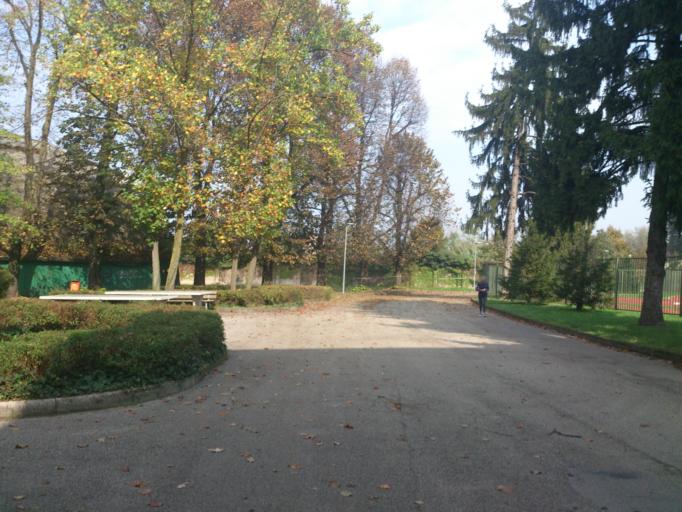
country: IT
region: Lombardy
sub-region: Citta metropolitana di Milano
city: San Donato Milanese
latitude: 45.4286
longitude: 9.2588
